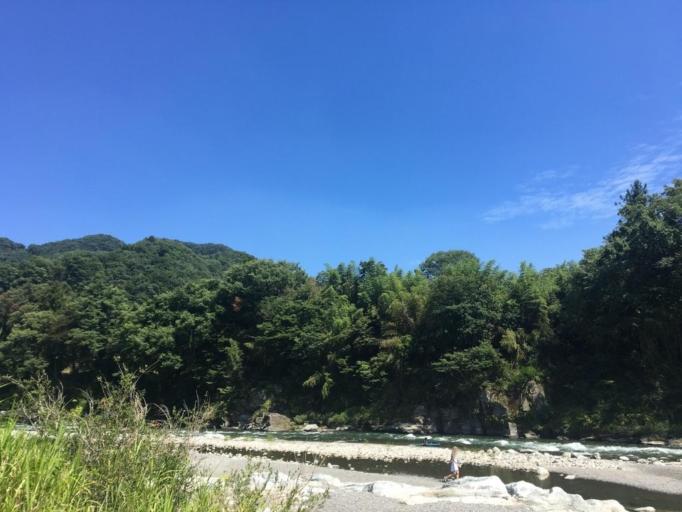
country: JP
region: Saitama
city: Yorii
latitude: 36.0849
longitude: 139.1158
